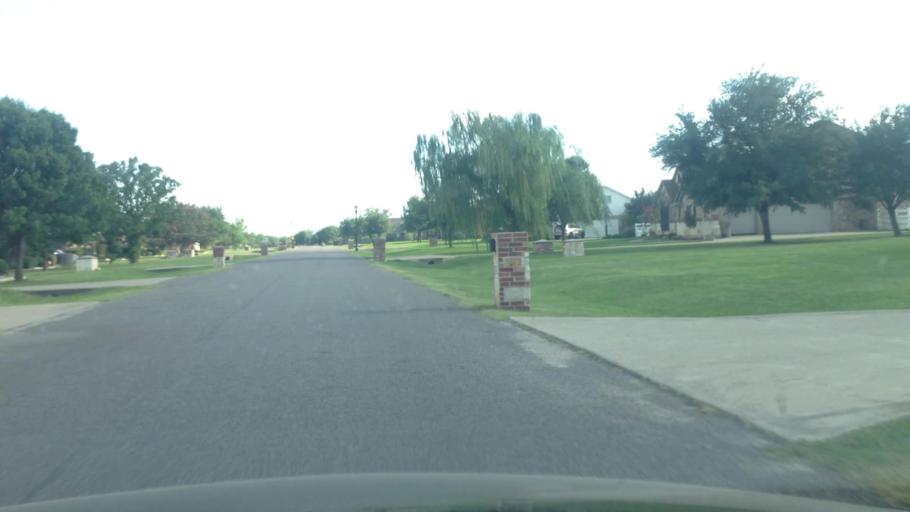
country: US
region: Texas
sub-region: Tarrant County
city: Haslet
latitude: 32.9679
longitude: -97.4005
